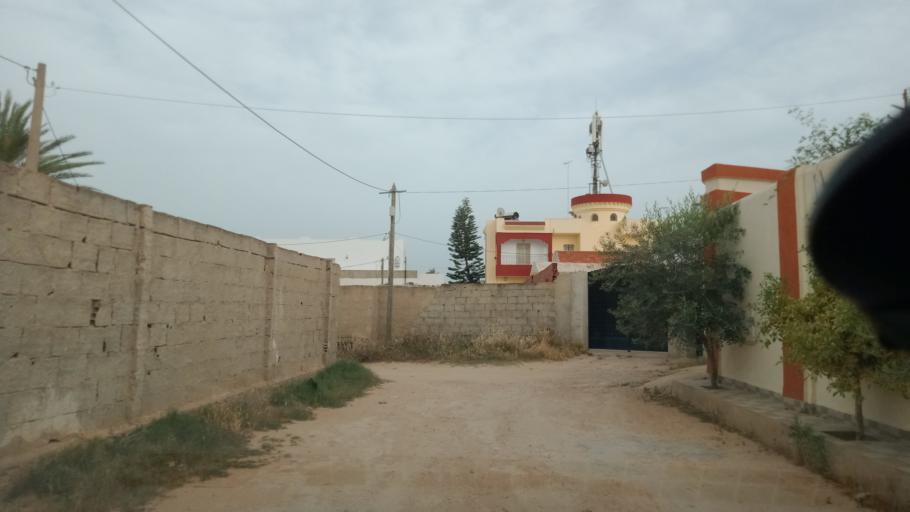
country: TN
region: Safaqis
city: Al Qarmadah
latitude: 34.7886
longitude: 10.7657
